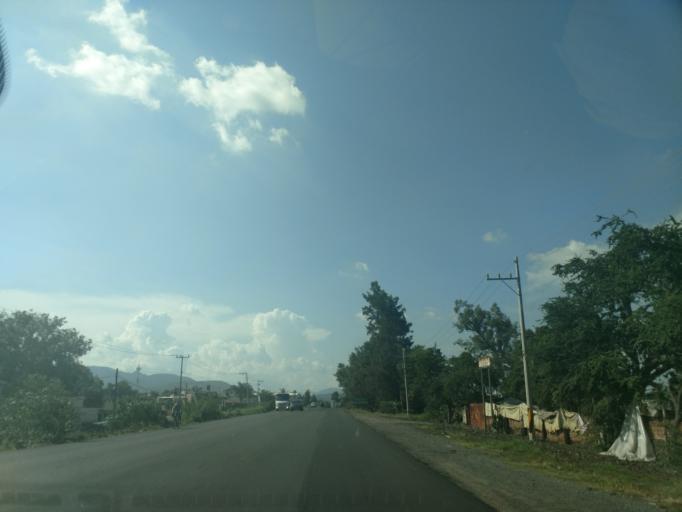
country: MX
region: Jalisco
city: Ahualulco de Mercado
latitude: 20.7003
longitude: -103.9662
